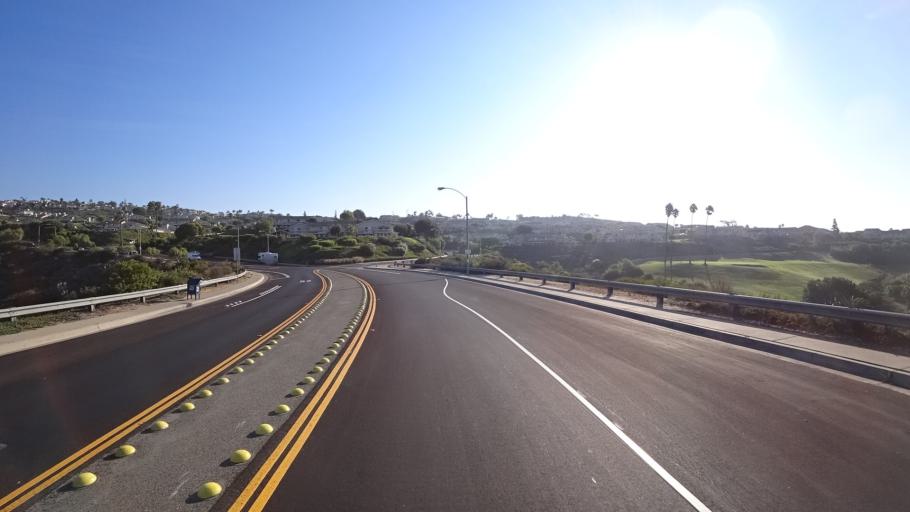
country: US
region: California
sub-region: Orange County
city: San Clemente
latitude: 33.4147
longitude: -117.5955
